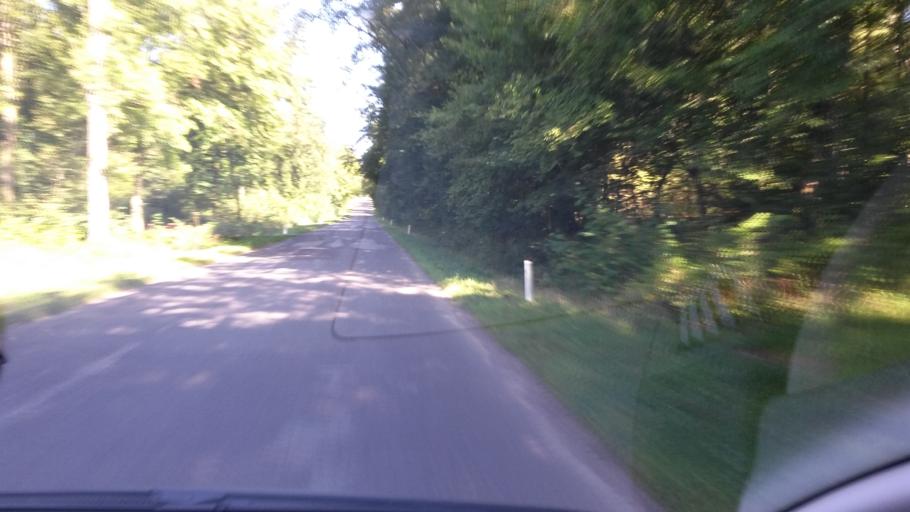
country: BE
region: Wallonia
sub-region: Province du Luxembourg
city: Neufchateau
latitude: 49.7970
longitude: 5.4168
